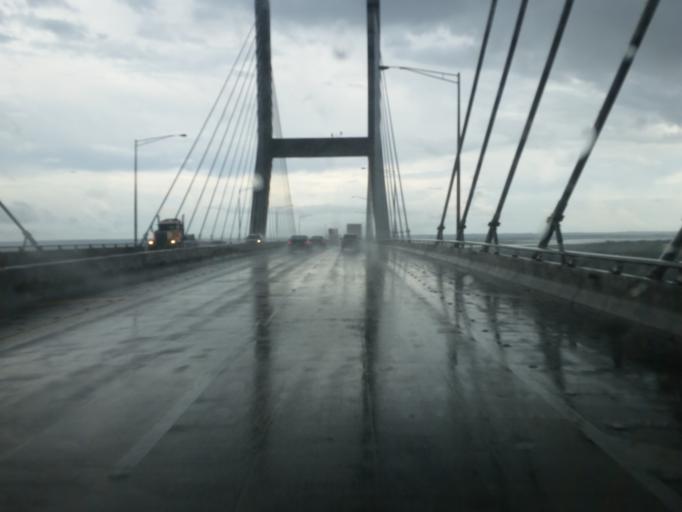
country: US
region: Alabama
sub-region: Mobile County
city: Prichard
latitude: 30.7336
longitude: -88.0434
